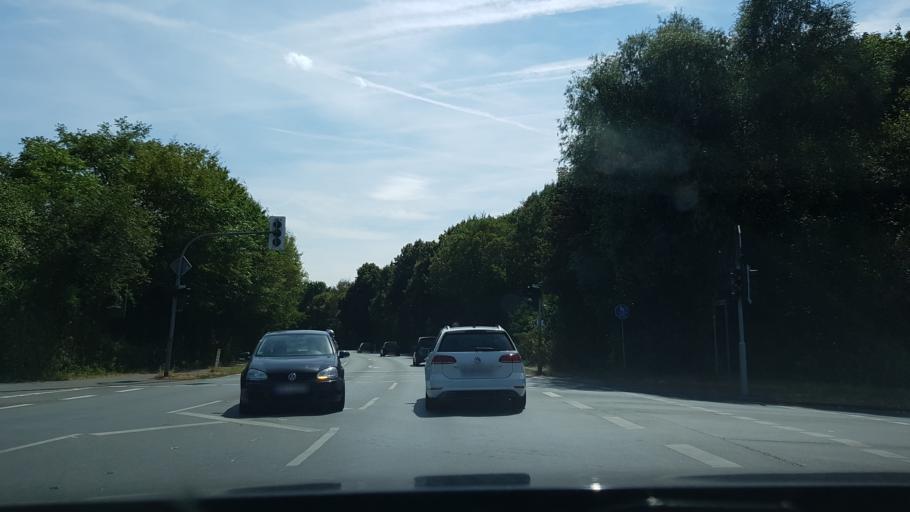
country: DE
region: North Rhine-Westphalia
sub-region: Regierungsbezirk Dusseldorf
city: Dinslaken
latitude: 51.5573
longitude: 6.7244
